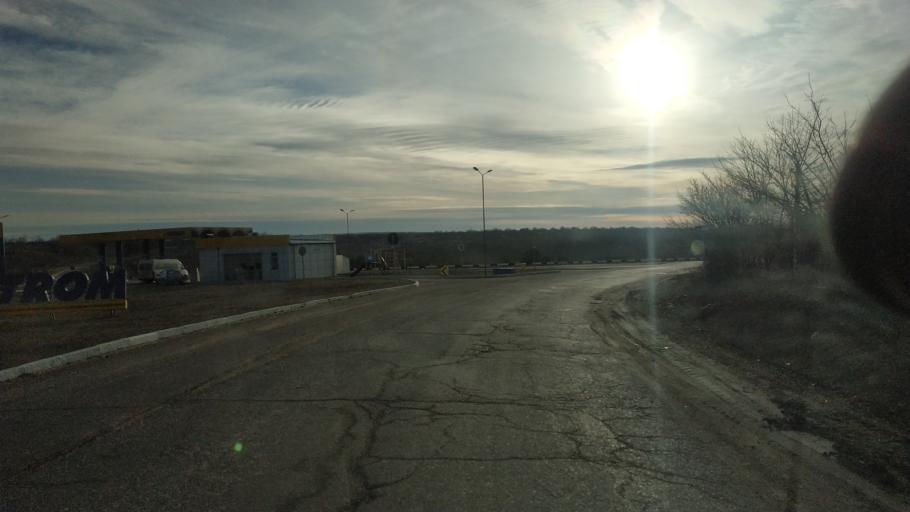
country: MD
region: Chisinau
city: Vadul lui Voda
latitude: 47.0707
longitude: 29.0166
